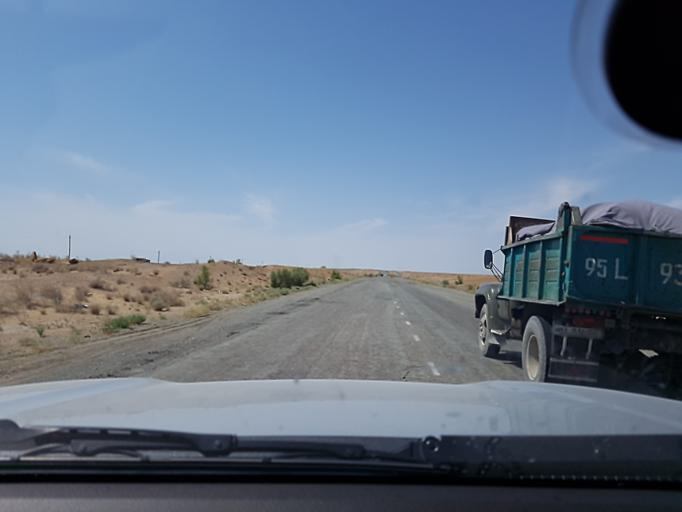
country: UZ
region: Karakalpakstan
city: Mang'it Shahri
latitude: 42.2880
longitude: 60.0767
